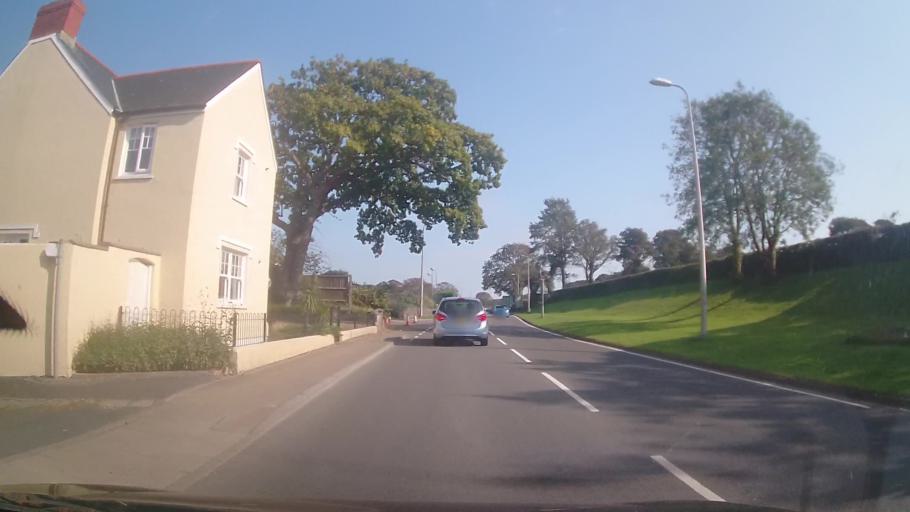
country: GB
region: Wales
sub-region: Pembrokeshire
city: Newport
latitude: 52.0167
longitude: -4.8290
